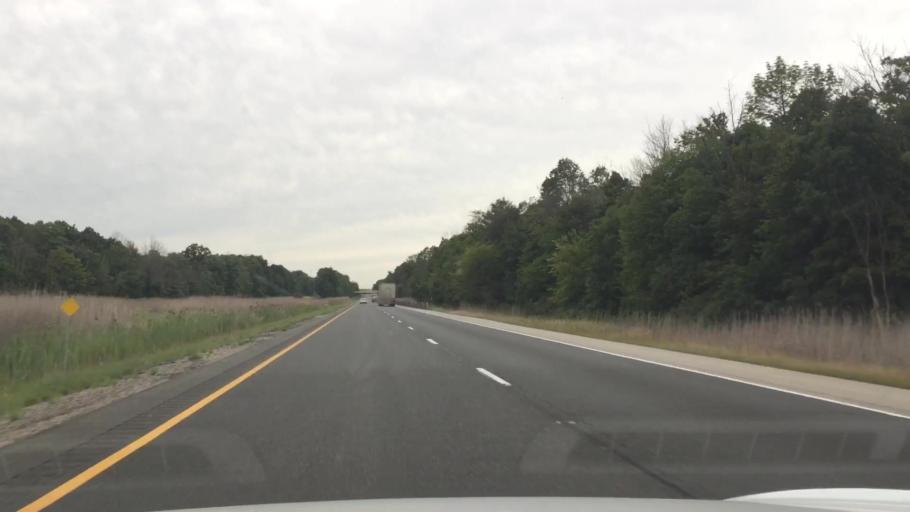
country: CA
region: Ontario
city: Lambton Shores
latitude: 42.9923
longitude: -81.7748
